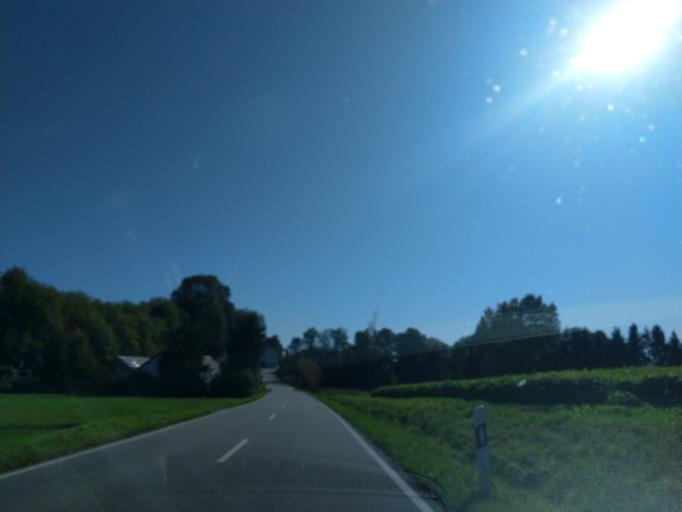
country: DE
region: Bavaria
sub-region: Lower Bavaria
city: Mariaposching
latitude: 48.8292
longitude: 12.7748
